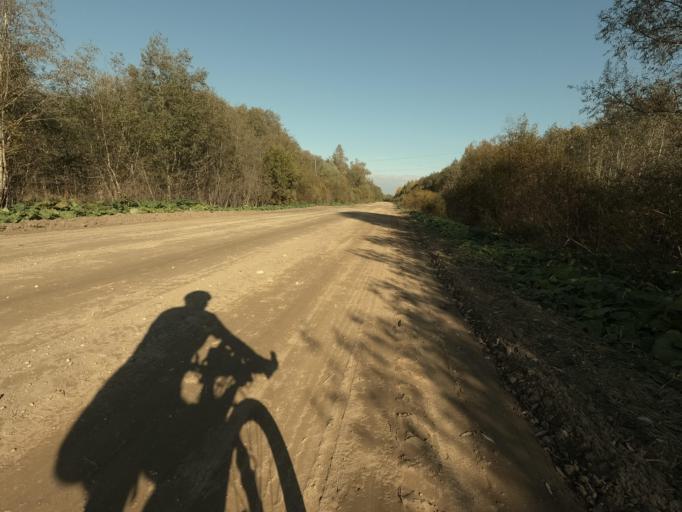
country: RU
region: Novgorod
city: Batetskiy
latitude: 58.8741
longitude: 30.7248
